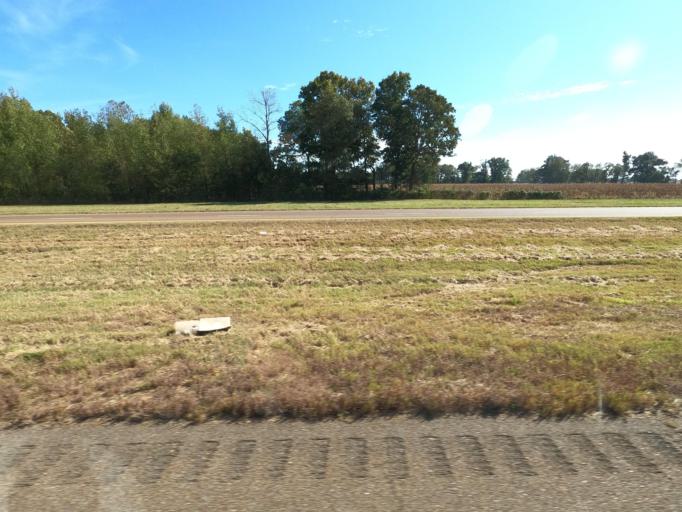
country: US
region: Tennessee
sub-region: Obion County
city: Union City
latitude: 36.4698
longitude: -88.9693
